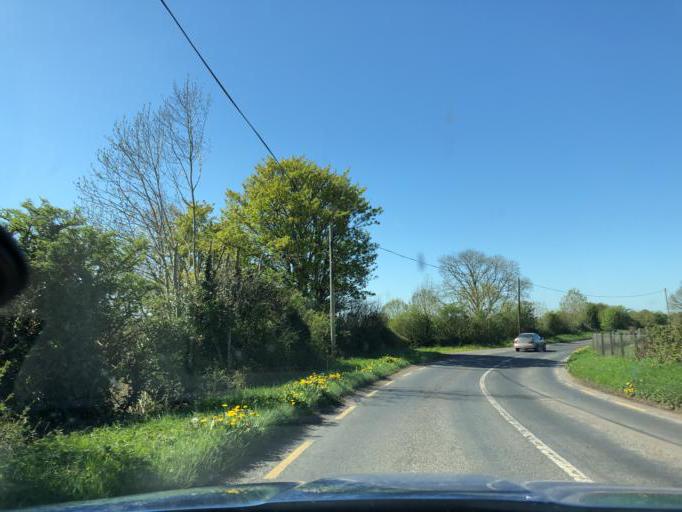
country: IE
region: Leinster
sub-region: Uibh Fhaili
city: Banagher
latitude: 53.2002
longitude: -8.1174
